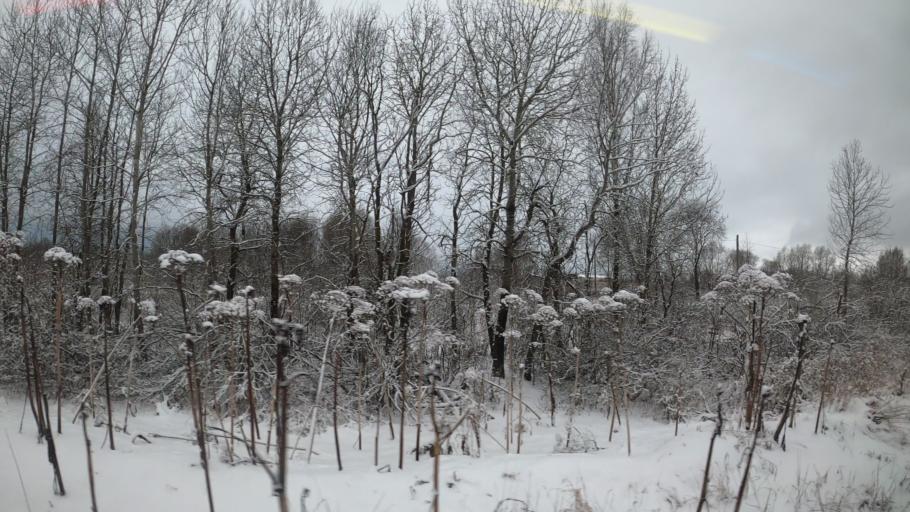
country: RU
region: Jaroslavl
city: Pereslavl'-Zalesskiy
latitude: 56.7321
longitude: 38.8996
